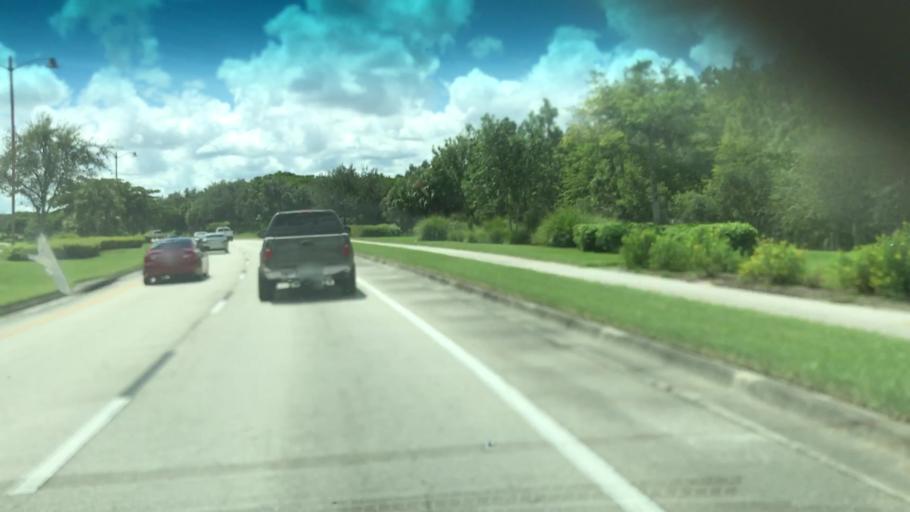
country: US
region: Florida
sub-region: Lee County
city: Estero
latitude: 26.4173
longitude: -81.7883
